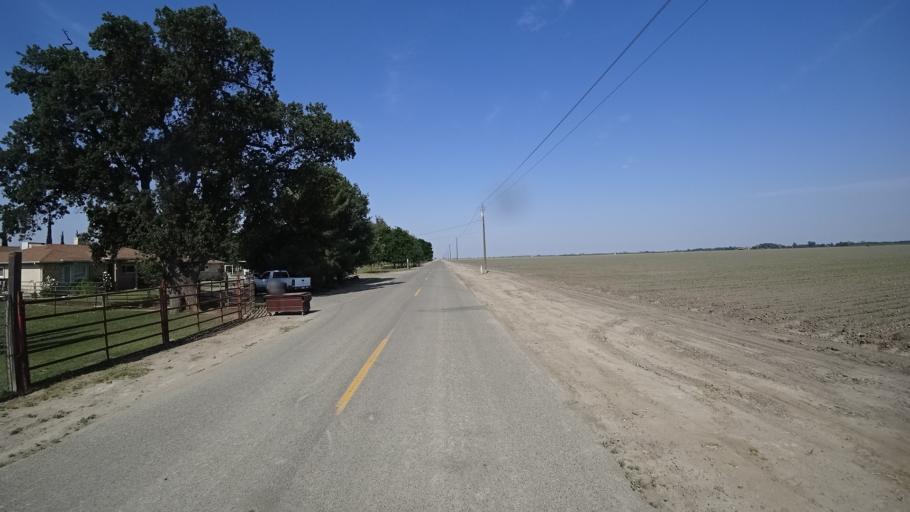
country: US
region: California
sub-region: Kings County
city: Lemoore
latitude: 36.3135
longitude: -119.8321
